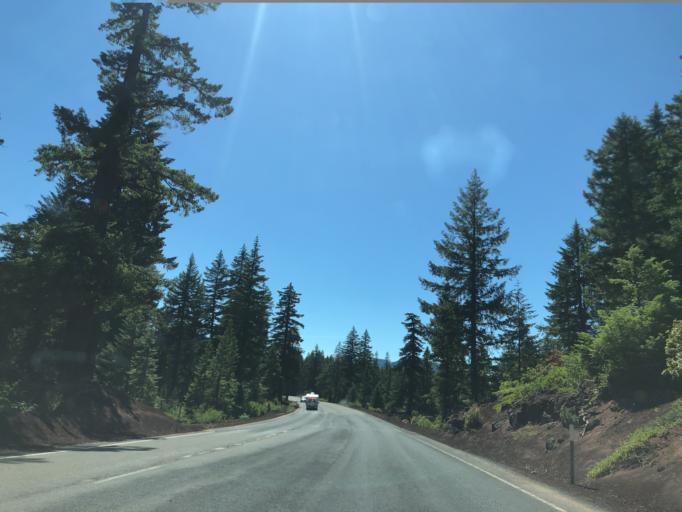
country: US
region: Oregon
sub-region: Deschutes County
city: Sisters
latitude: 44.4325
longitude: -121.9690
